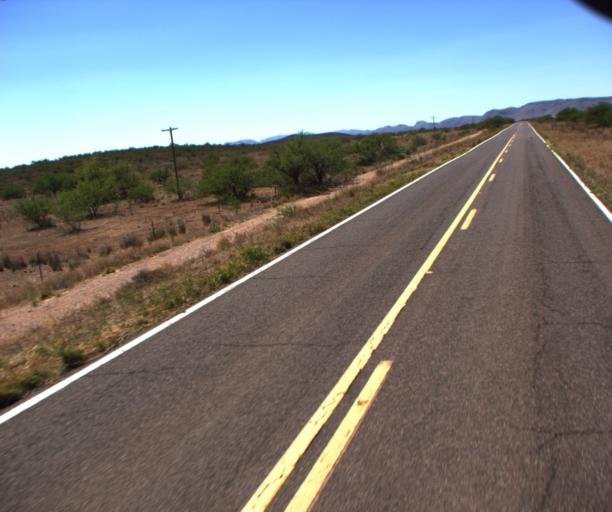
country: US
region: Arizona
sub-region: Cochise County
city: Douglas
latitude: 31.5117
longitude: -109.3112
